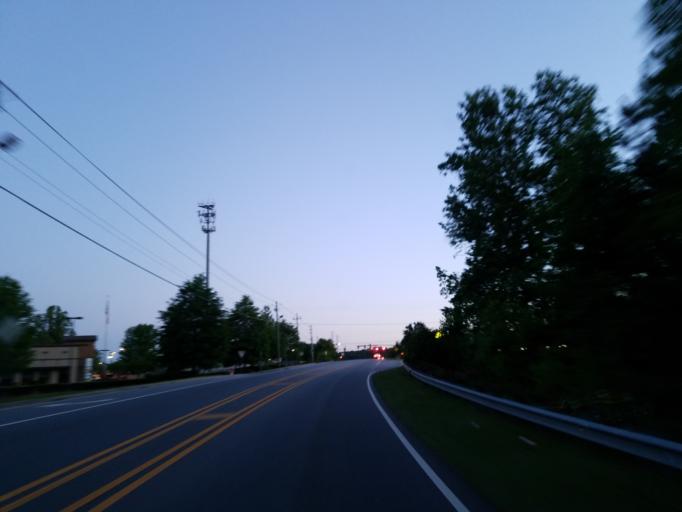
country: US
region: Georgia
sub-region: Lumpkin County
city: Dahlonega
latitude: 34.5351
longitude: -83.9761
